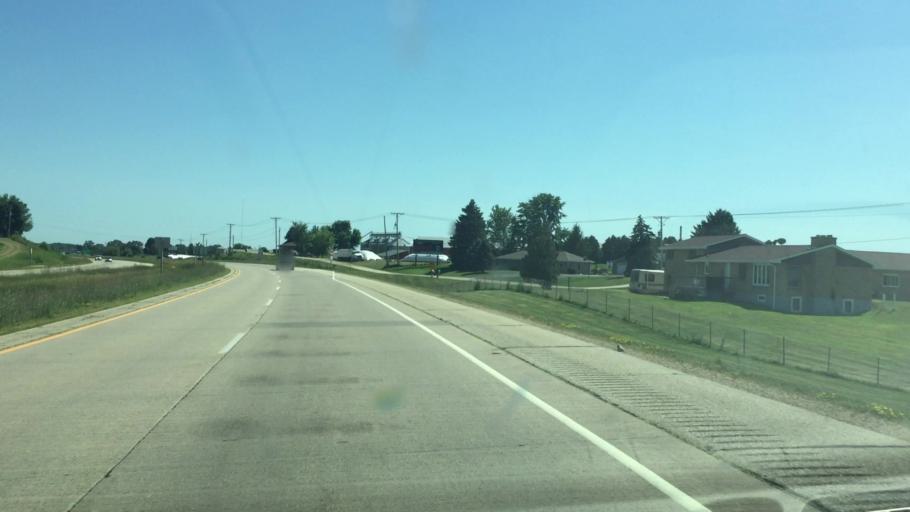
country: US
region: Wisconsin
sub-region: Grant County
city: Dickeyville
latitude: 42.5714
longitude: -90.6122
